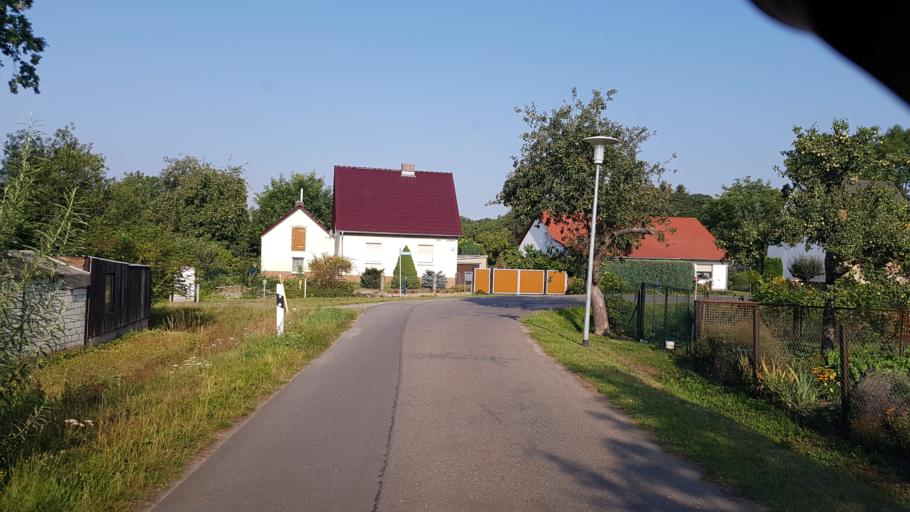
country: DE
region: Brandenburg
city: Drebkau
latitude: 51.6921
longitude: 14.2503
